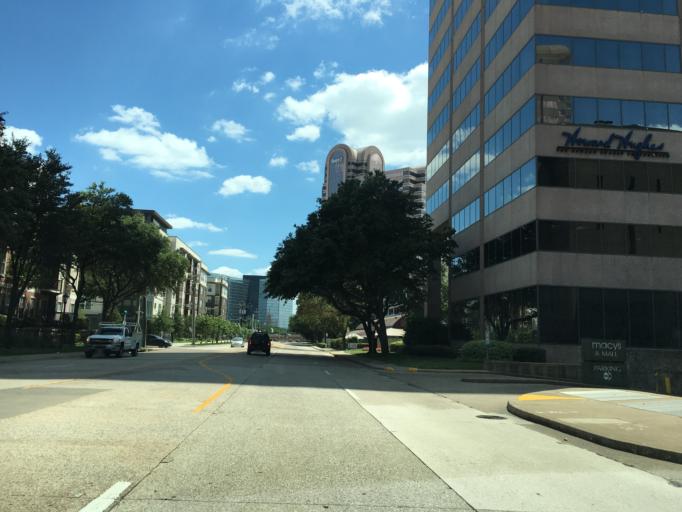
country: US
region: Texas
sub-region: Dallas County
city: Addison
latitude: 32.9299
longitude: -96.8180
